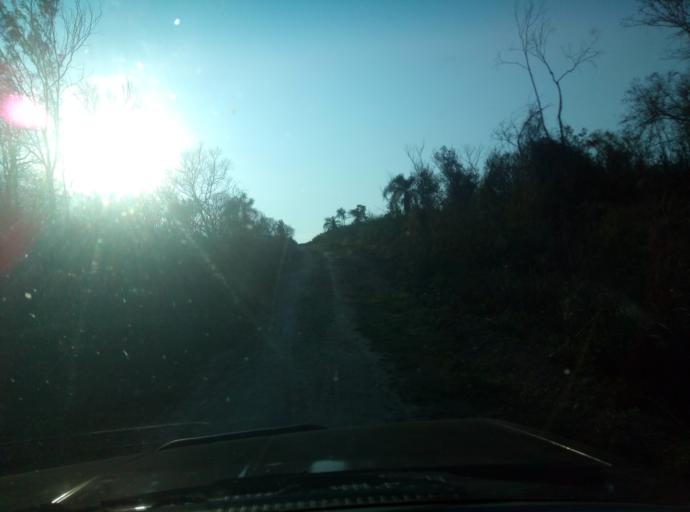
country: PY
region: Caaguazu
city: Doctor Cecilio Baez
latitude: -25.1988
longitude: -56.1249
